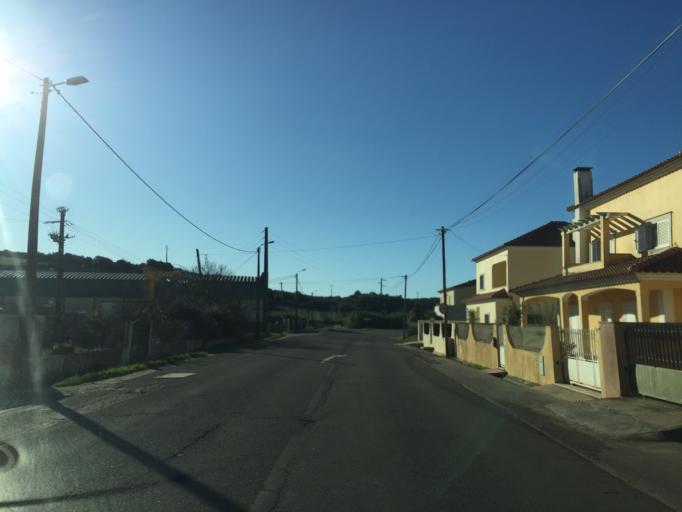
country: PT
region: Lisbon
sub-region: Sintra
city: Pero Pinheiro
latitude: 38.8662
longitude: -9.2991
